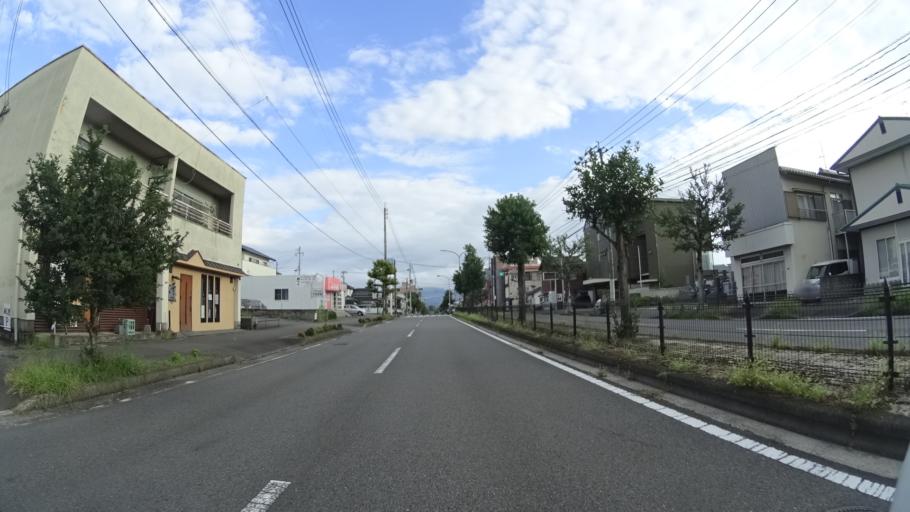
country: JP
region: Oita
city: Beppu
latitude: 33.2965
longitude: 131.4955
